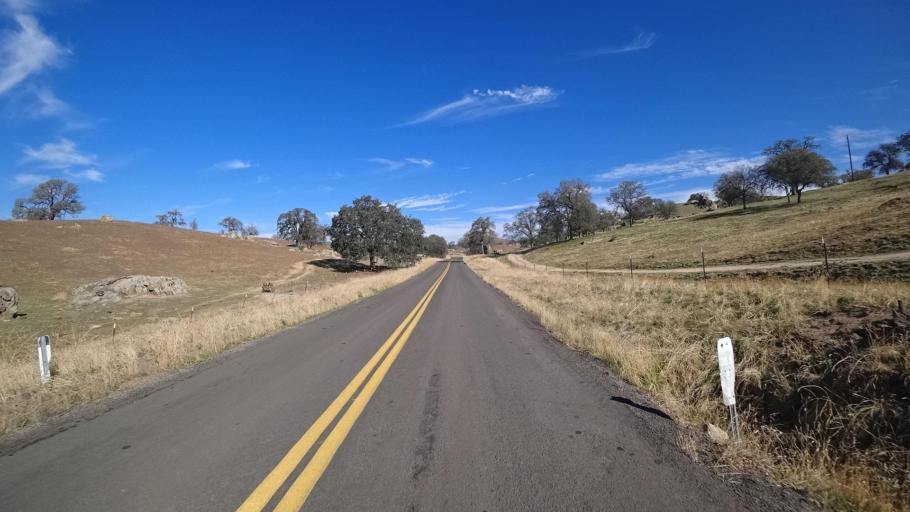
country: US
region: California
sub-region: Kern County
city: Oildale
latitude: 35.6238
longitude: -118.8492
